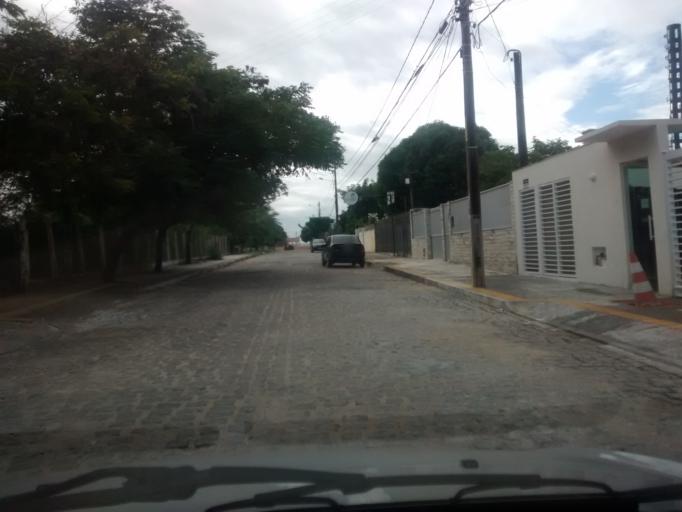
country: BR
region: Rio Grande do Norte
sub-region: Natal
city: Natal
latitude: -5.8752
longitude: -35.1807
